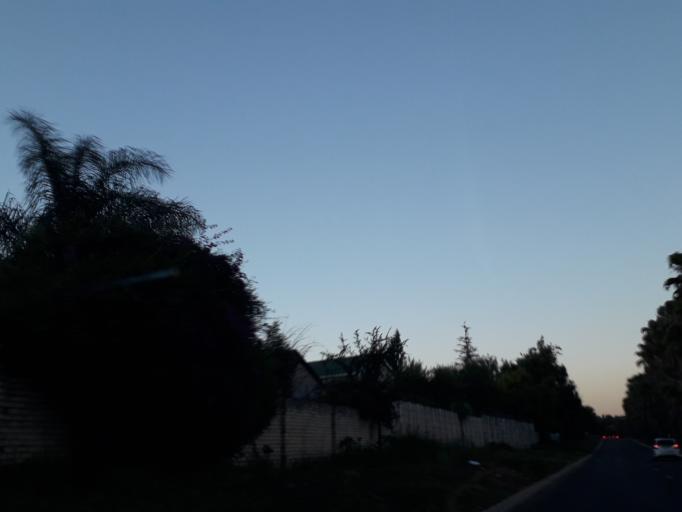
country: ZA
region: Gauteng
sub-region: City of Johannesburg Metropolitan Municipality
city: Roodepoort
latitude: -26.1323
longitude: 27.9303
